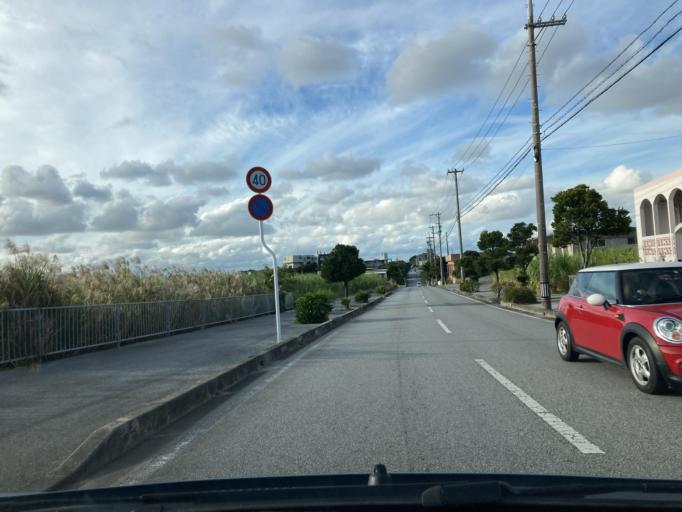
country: JP
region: Okinawa
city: Itoman
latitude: 26.1388
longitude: 127.7371
